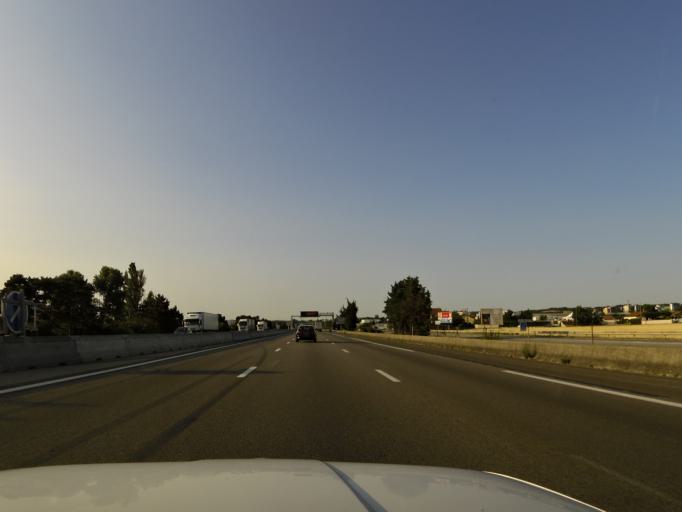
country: FR
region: Rhone-Alpes
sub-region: Departement de la Drome
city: Portes-les-Valence
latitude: 44.8816
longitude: 4.8671
